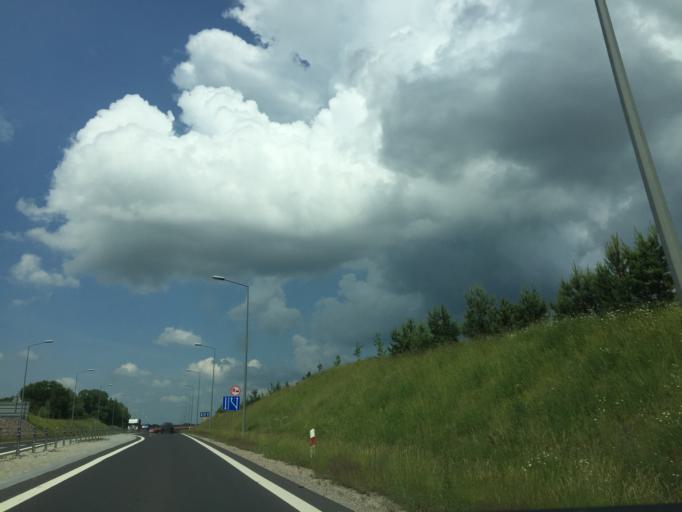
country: PL
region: Warmian-Masurian Voivodeship
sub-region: Powiat olecki
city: Olecko
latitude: 54.0442
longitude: 22.4703
